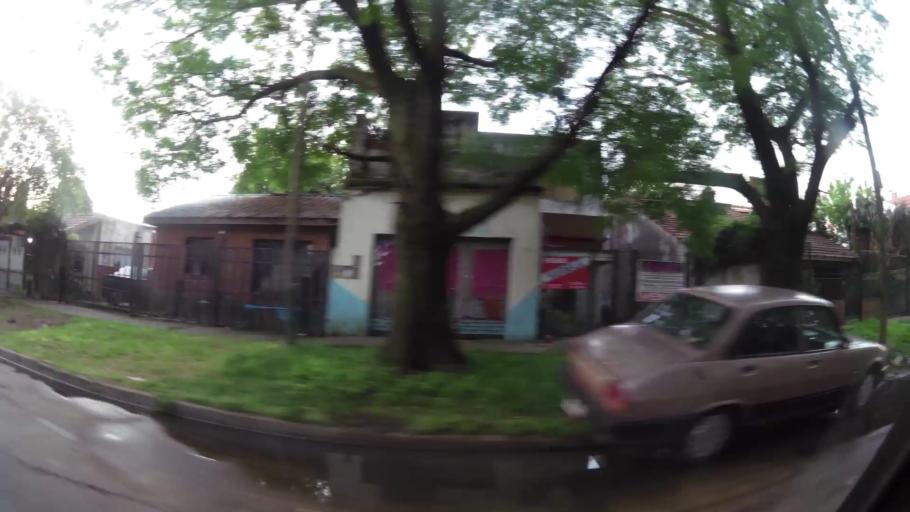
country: AR
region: Buenos Aires
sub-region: Partido de Lomas de Zamora
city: Lomas de Zamora
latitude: -34.7659
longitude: -58.3745
